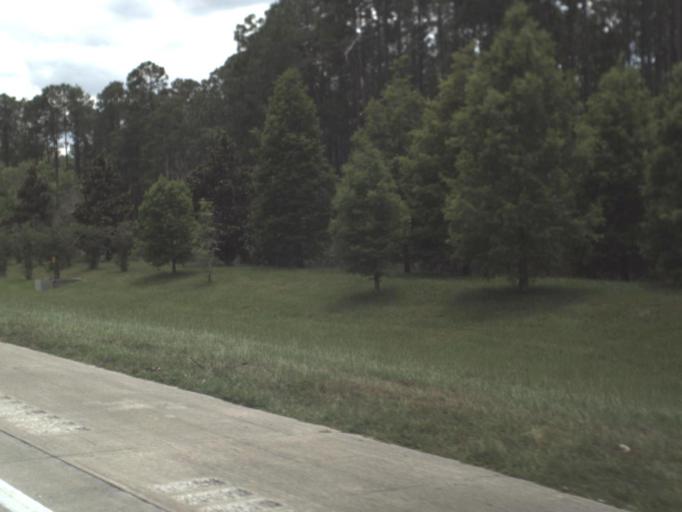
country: US
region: Florida
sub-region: Saint Johns County
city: Palm Valley
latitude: 30.2035
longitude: -81.5140
